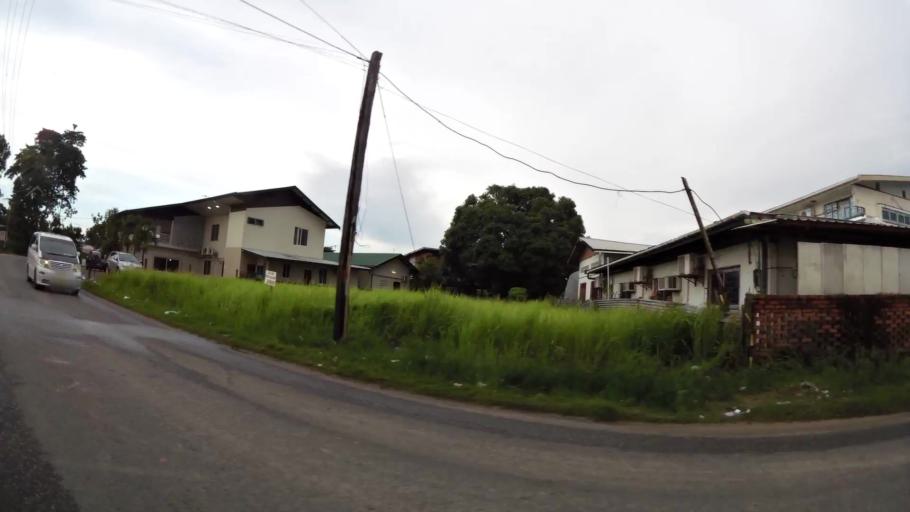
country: SR
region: Paramaribo
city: Paramaribo
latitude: 5.8240
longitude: -55.2058
